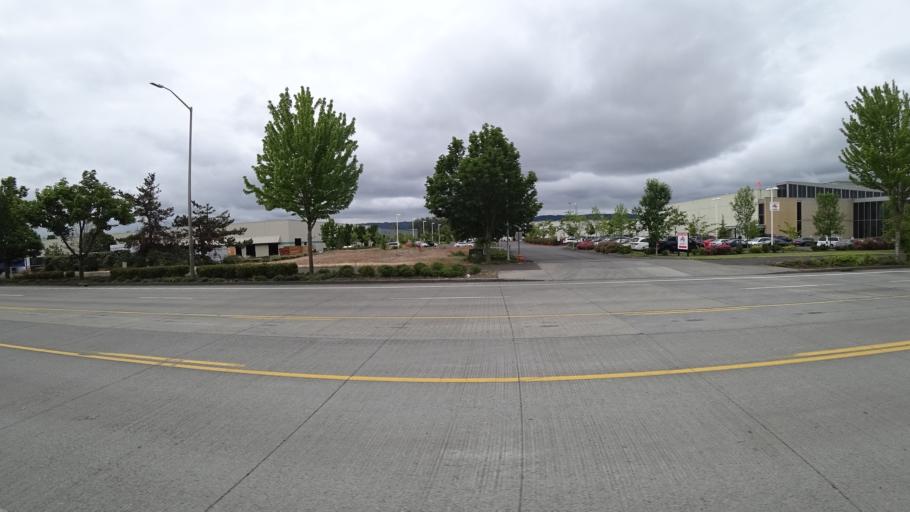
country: US
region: Washington
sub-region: Clark County
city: Lake Shore
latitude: 45.6323
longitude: -122.7487
